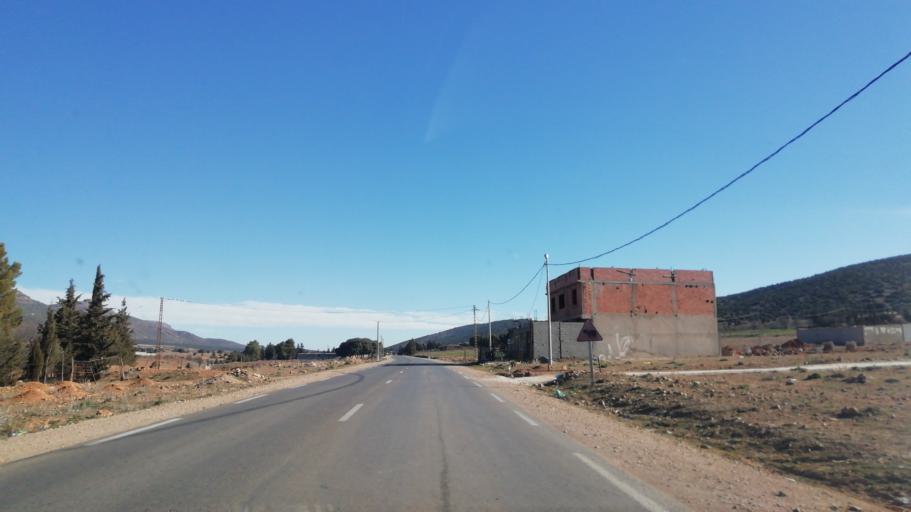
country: DZ
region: Tlemcen
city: Sebdou
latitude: 34.6782
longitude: -1.2619
